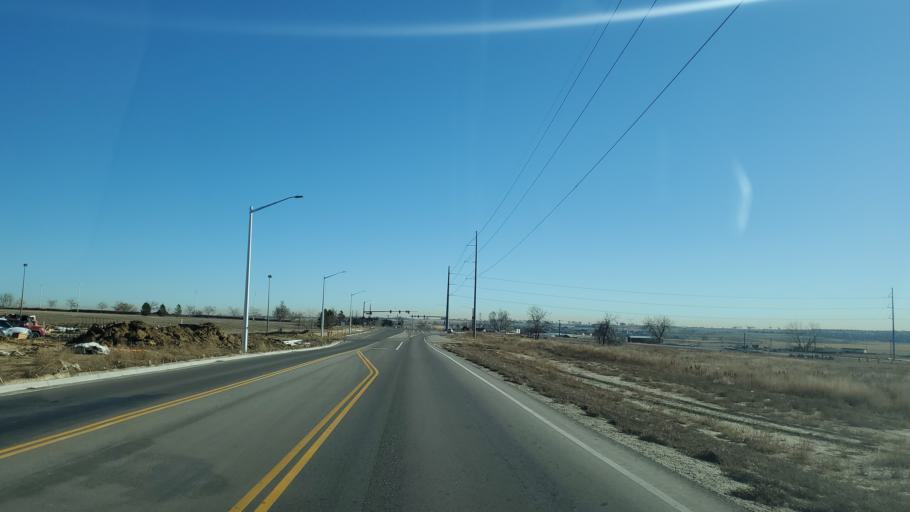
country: US
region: Colorado
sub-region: Boulder County
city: Erie
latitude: 39.9866
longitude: -104.9821
